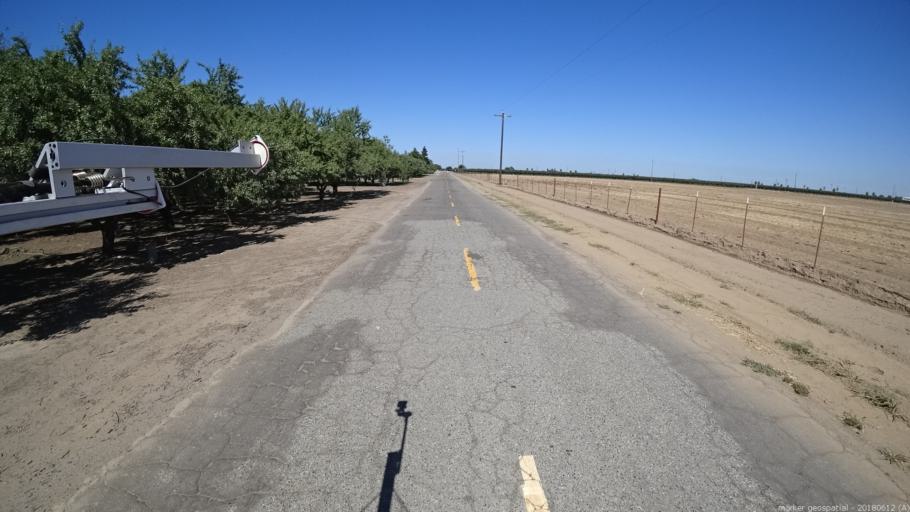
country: US
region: California
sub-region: Madera County
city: Chowchilla
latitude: 37.0327
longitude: -120.3259
